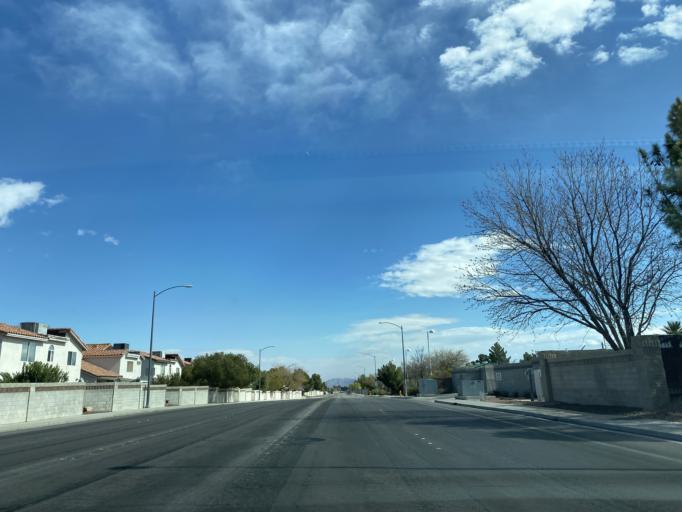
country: US
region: Nevada
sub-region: Clark County
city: Summerlin South
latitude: 36.2262
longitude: -115.2863
